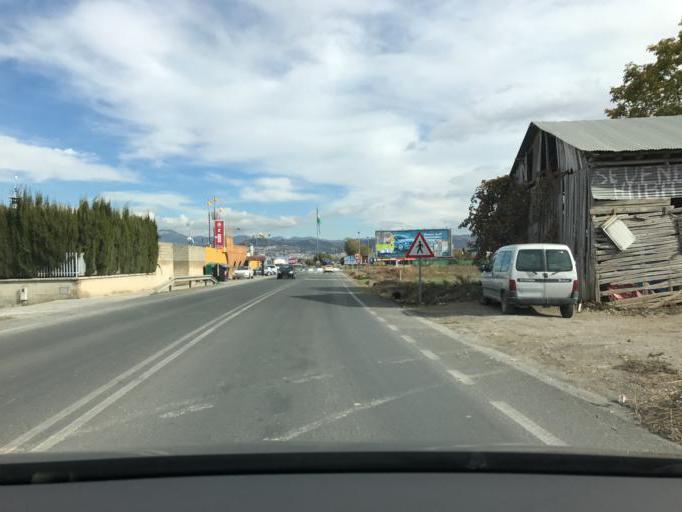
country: ES
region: Andalusia
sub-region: Provincia de Granada
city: Churriana de la Vega
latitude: 37.1522
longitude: -3.6509
